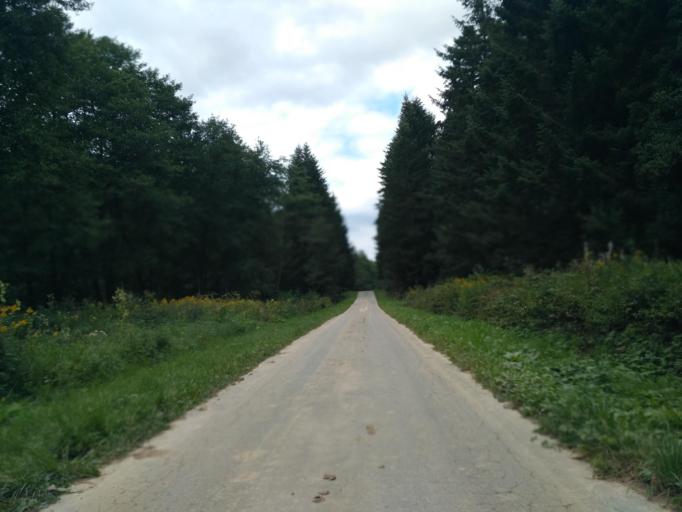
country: PL
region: Subcarpathian Voivodeship
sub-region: Powiat rzeszowski
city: Dynow
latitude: 49.7472
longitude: 22.3010
